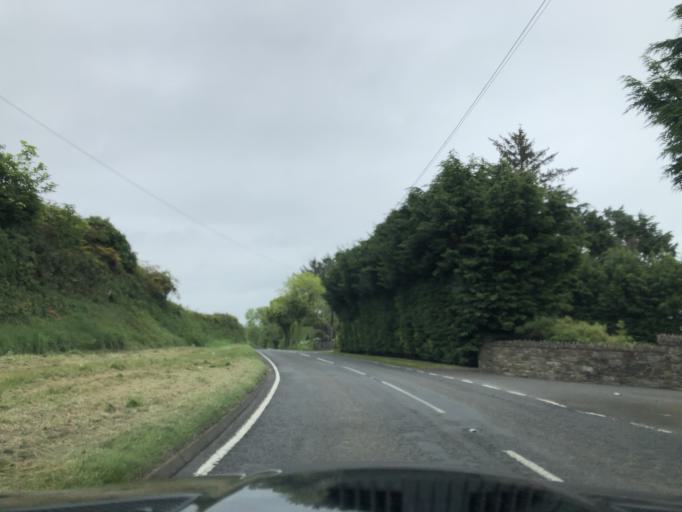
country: GB
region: Northern Ireland
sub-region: Down District
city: Portaferry
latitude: 54.3596
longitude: -5.5727
